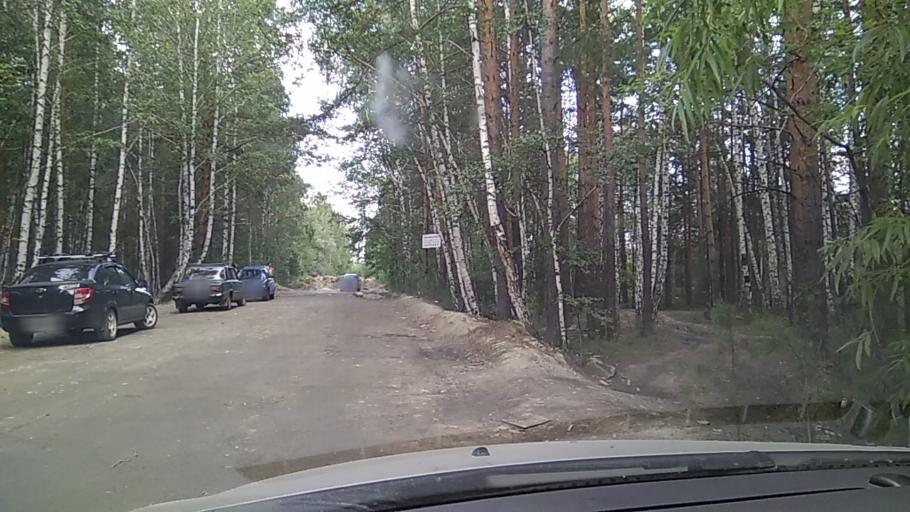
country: RU
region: Chelyabinsk
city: Kyshtym
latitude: 55.6772
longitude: 60.5893
